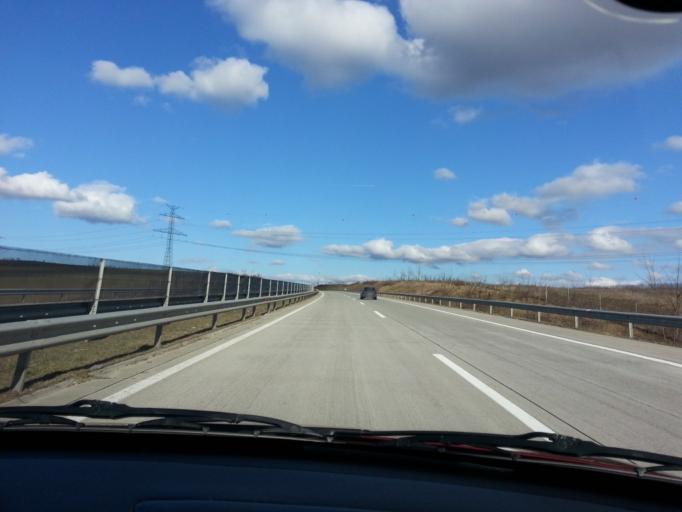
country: HU
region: Pest
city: Nagytarcsa
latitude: 47.5460
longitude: 19.3125
